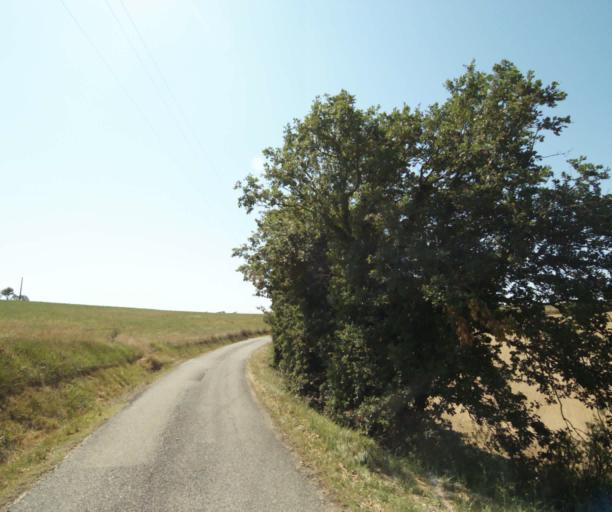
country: FR
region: Midi-Pyrenees
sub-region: Departement de l'Ariege
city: Lezat-sur-Leze
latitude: 43.2723
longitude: 1.3761
